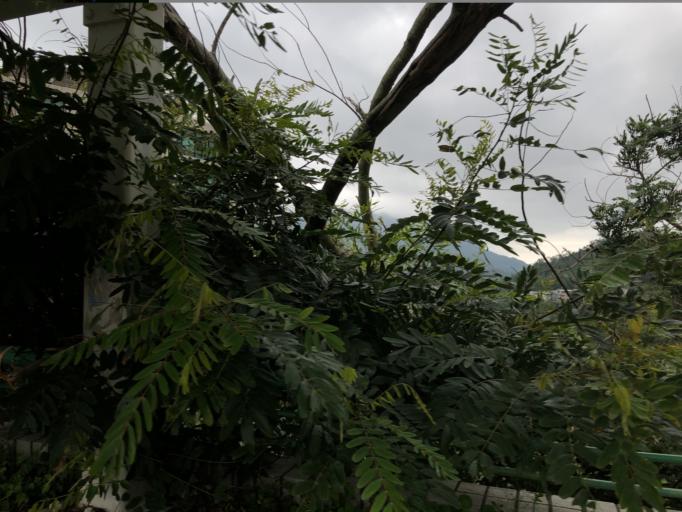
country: HK
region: Tai Po
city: Tai Po
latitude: 22.4663
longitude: 114.1938
